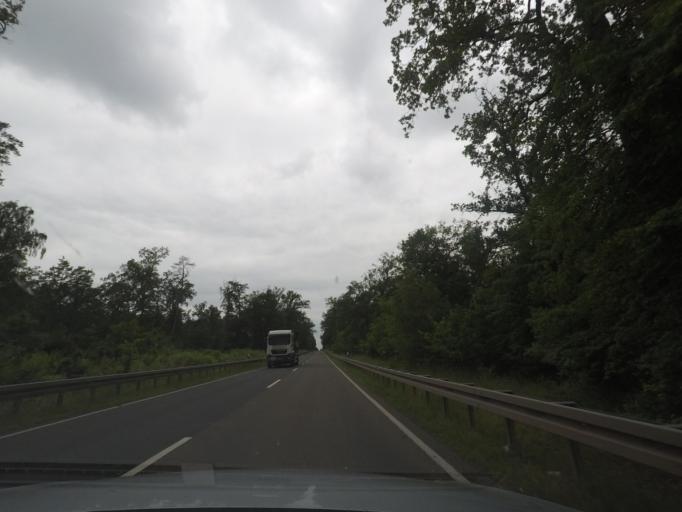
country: DE
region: Saxony-Anhalt
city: Colbitz
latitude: 52.3405
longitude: 11.5808
